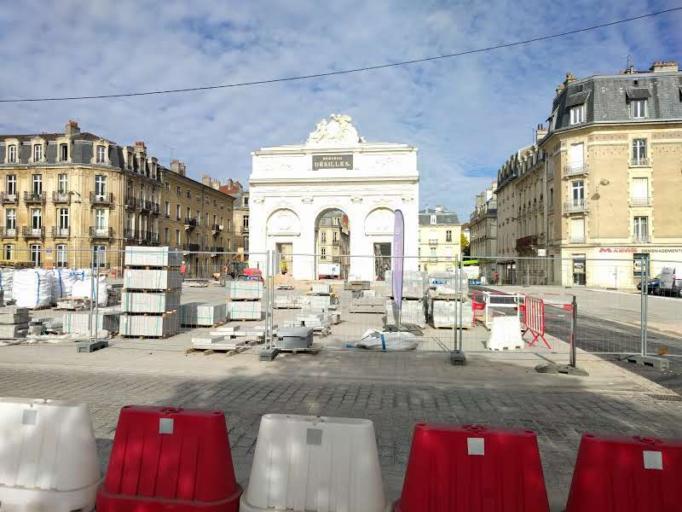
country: FR
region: Lorraine
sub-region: Departement de Meurthe-et-Moselle
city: Maxeville
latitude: 48.6976
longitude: 6.1746
